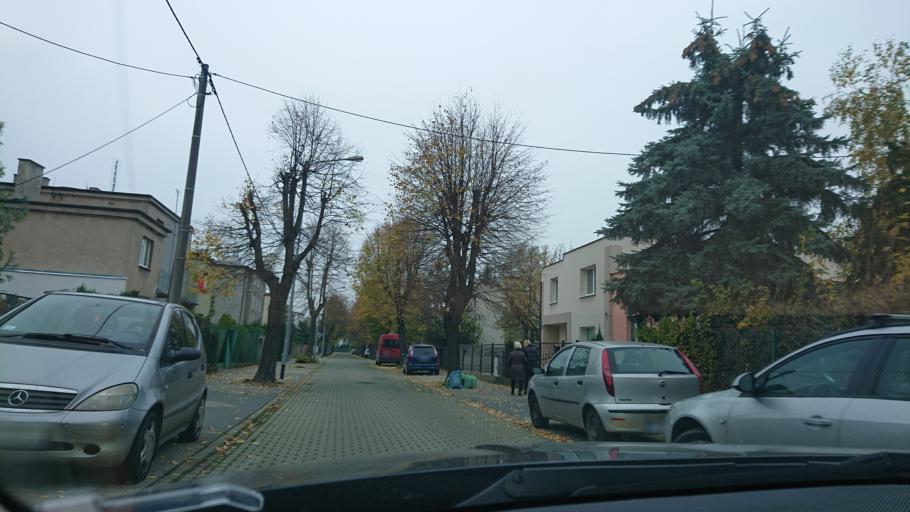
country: PL
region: Greater Poland Voivodeship
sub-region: Powiat gnieznienski
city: Gniezno
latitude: 52.5333
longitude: 17.6221
